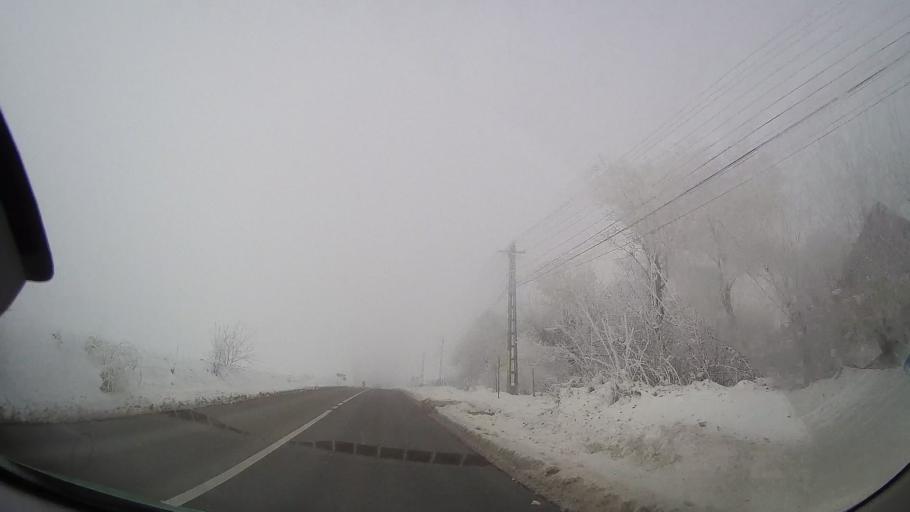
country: RO
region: Iasi
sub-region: Comuna Halaucesti
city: Halaucesti
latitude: 47.1029
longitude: 26.8144
